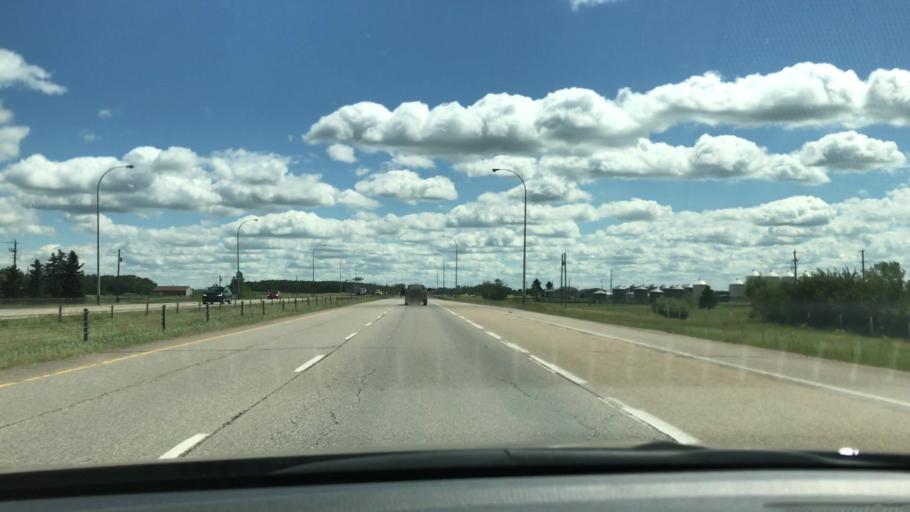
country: CA
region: Alberta
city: Leduc
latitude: 53.2523
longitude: -113.5619
